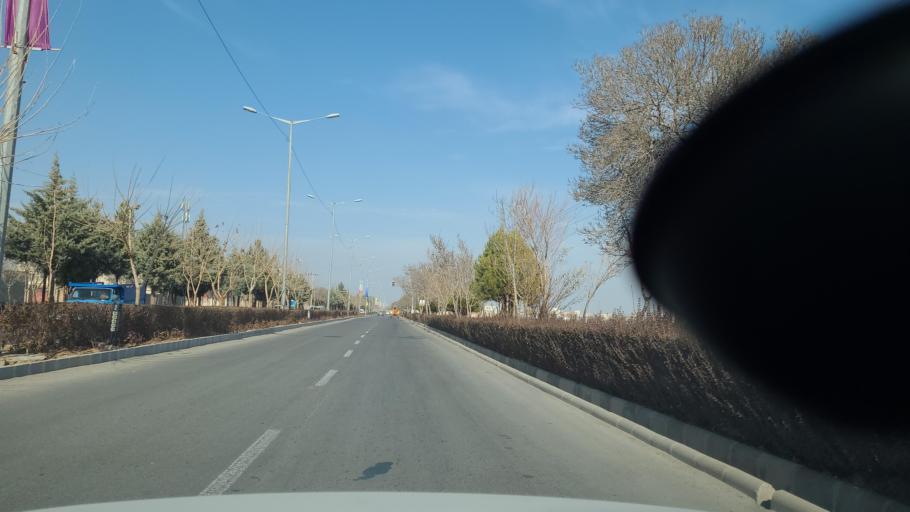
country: IR
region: Razavi Khorasan
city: Fariman
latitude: 35.6834
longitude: 59.8433
